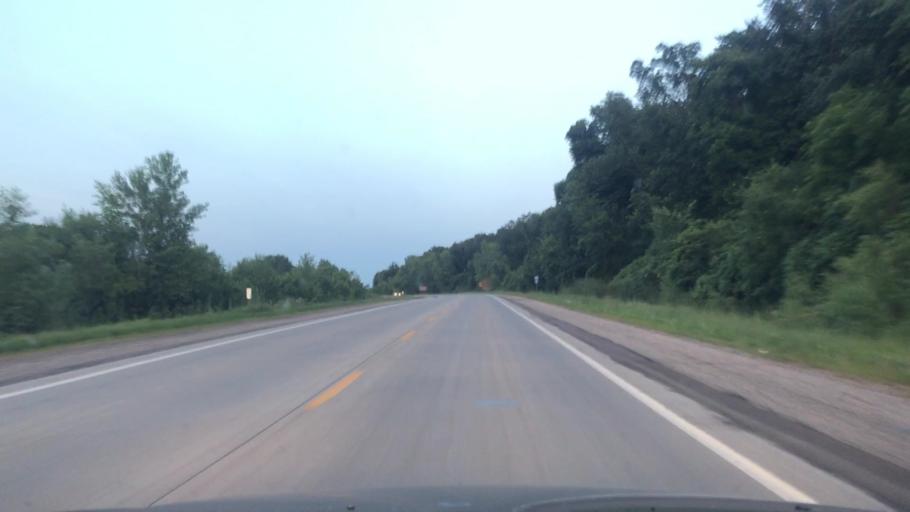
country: US
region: Minnesota
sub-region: Redwood County
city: Redwood Falls
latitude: 44.5409
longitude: -95.0131
